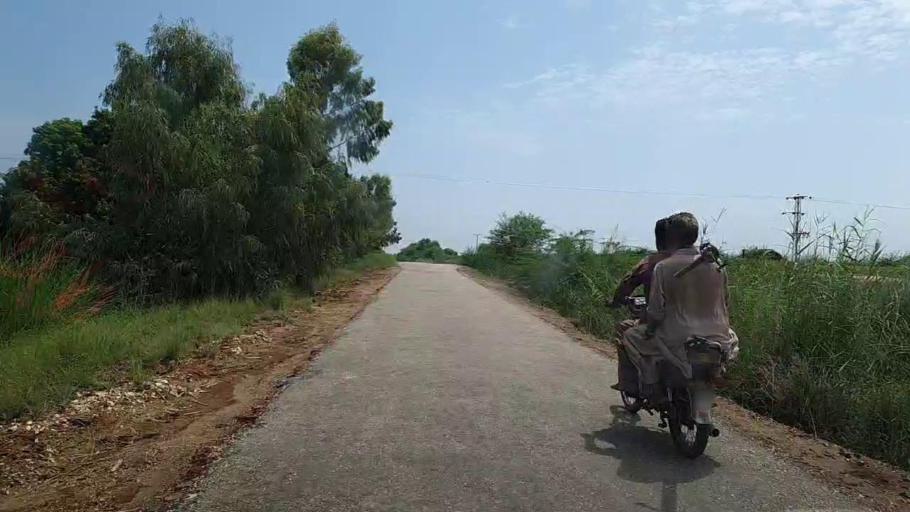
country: PK
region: Sindh
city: Bhiria
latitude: 26.9031
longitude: 68.1999
